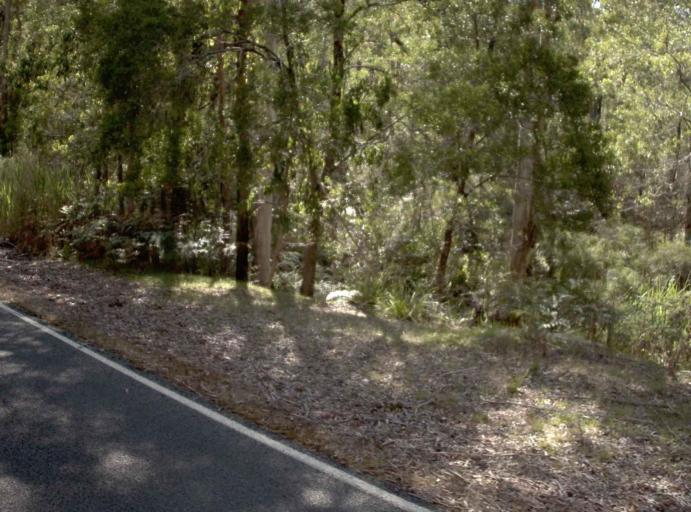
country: AU
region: New South Wales
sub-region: Bombala
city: Bombala
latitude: -37.3796
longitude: 148.6582
